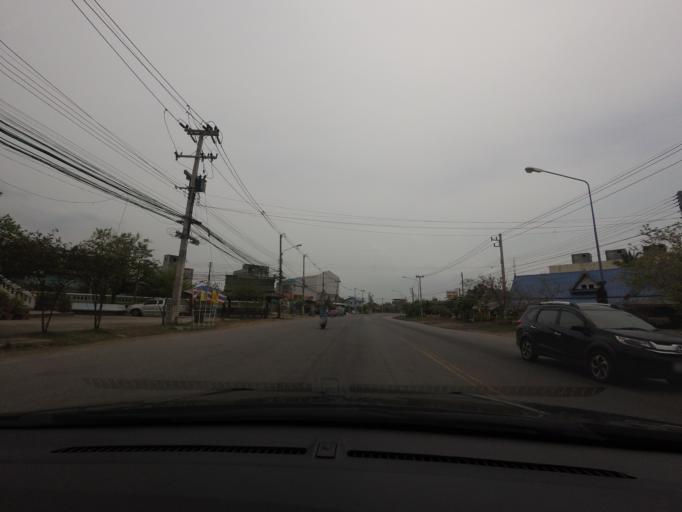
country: TH
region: Phetchaburi
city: Ban Laem
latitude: 13.2103
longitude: 99.9760
